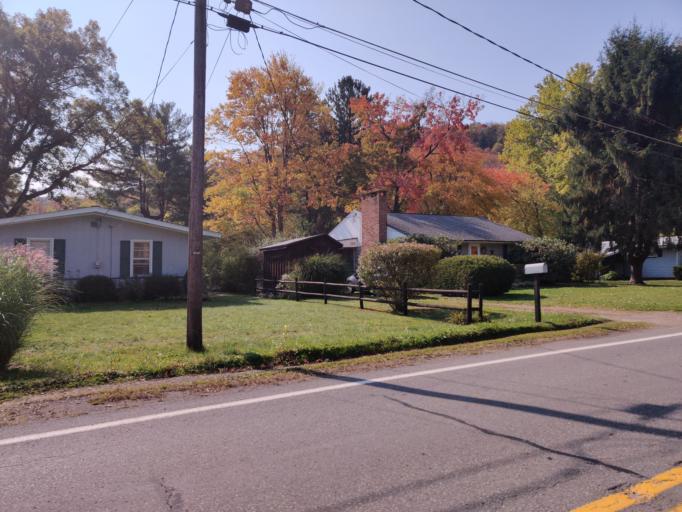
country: US
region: Pennsylvania
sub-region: Warren County
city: Warren
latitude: 41.8225
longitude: -79.1113
